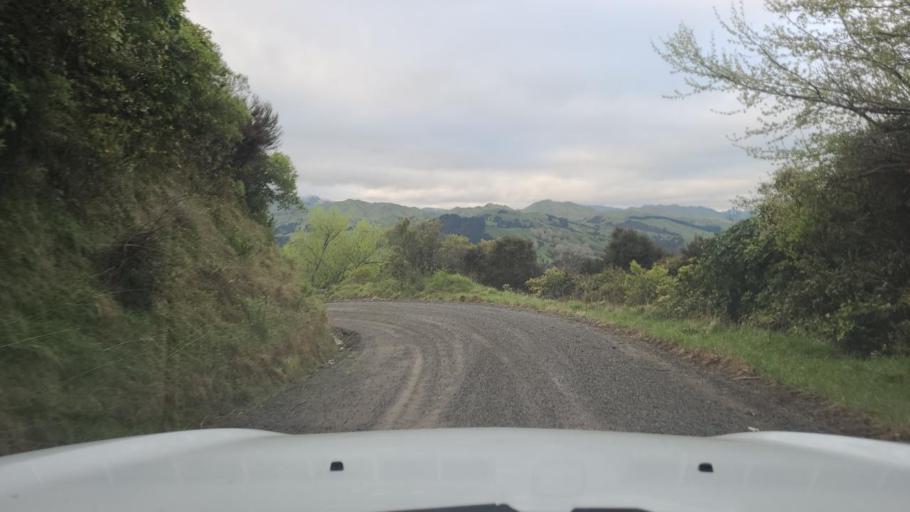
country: NZ
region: Wellington
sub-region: Masterton District
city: Masterton
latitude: -41.1629
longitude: 175.6853
